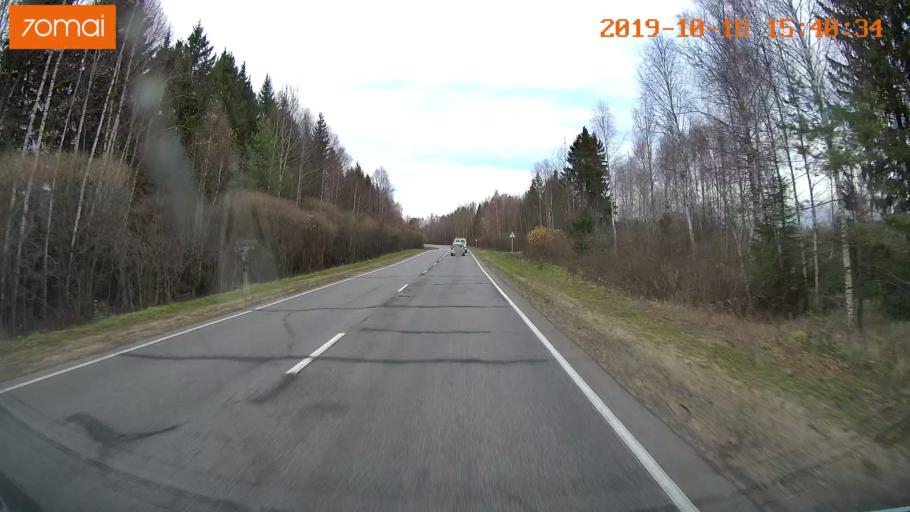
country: RU
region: Vladimir
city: Golovino
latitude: 55.9358
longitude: 40.5929
